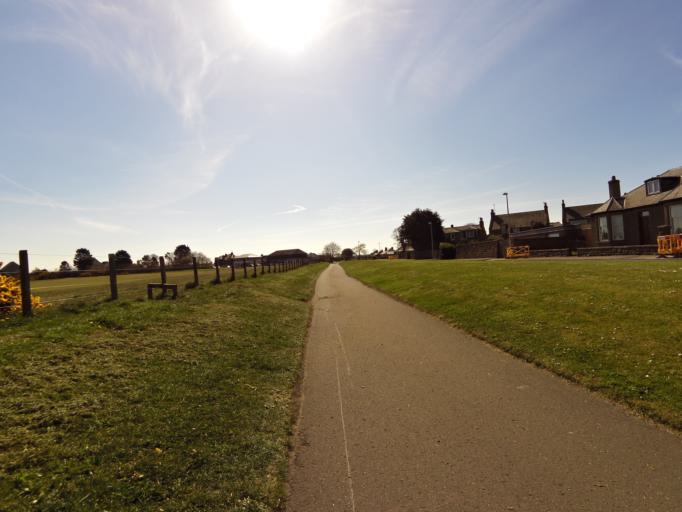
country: GB
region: Scotland
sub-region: Angus
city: Montrose
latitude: 56.7169
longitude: -2.4569
